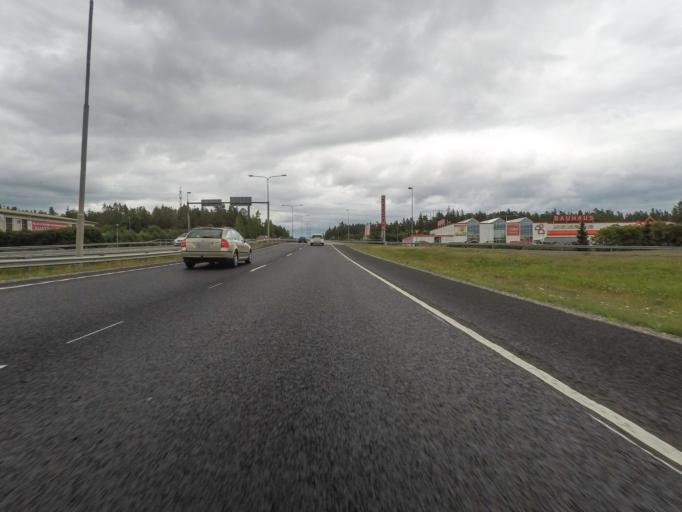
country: FI
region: Varsinais-Suomi
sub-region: Turku
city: Raisio
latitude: 60.4926
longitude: 22.2060
